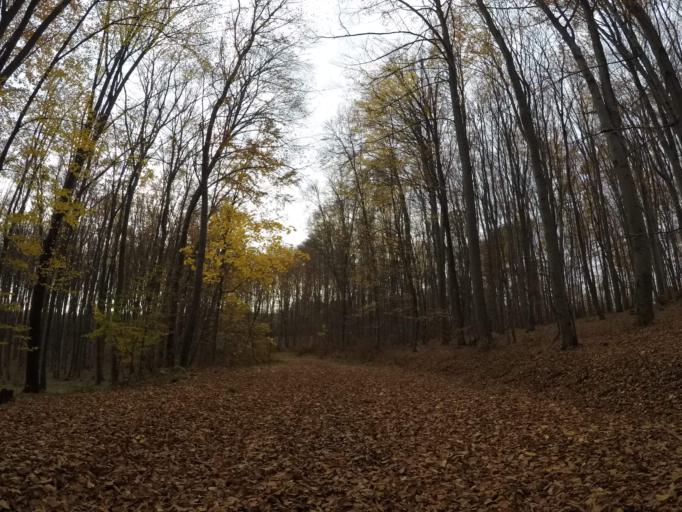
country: SK
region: Presovsky
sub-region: Okres Presov
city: Presov
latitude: 48.9682
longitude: 21.1846
